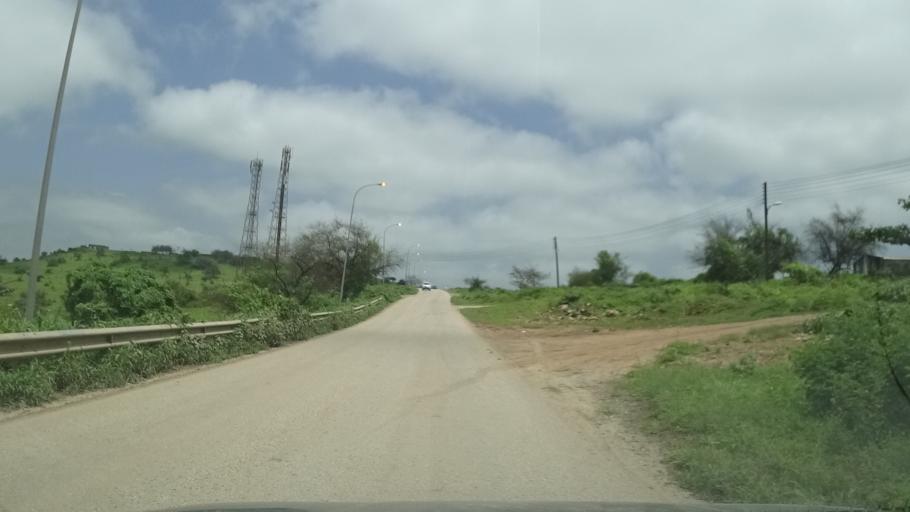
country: OM
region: Zufar
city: Salalah
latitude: 17.1859
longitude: 54.1605
